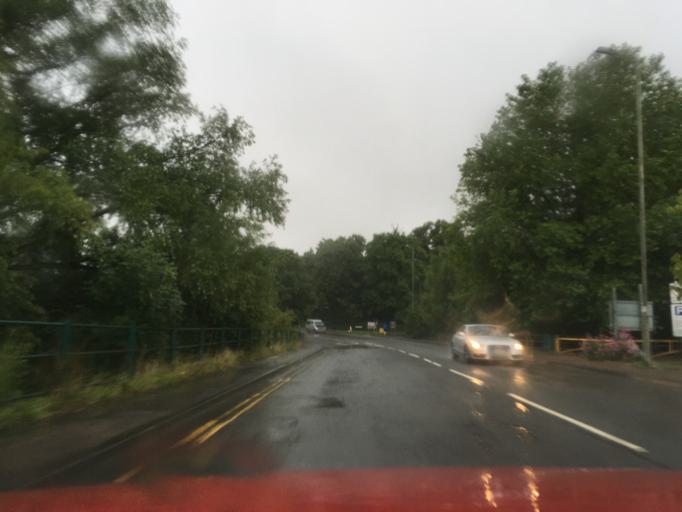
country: GB
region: England
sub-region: Gloucestershire
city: Tewkesbury
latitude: 51.9888
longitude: -2.1635
